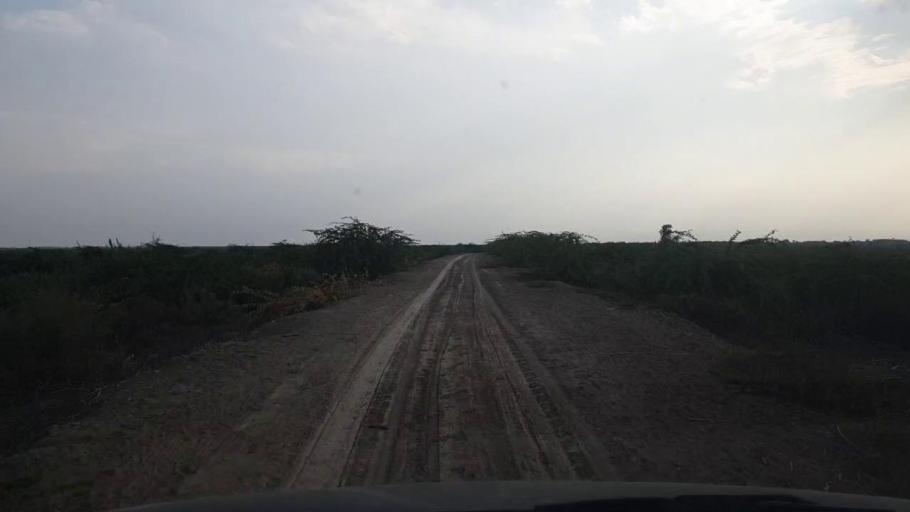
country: PK
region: Sindh
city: Badin
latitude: 24.4759
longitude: 68.6999
